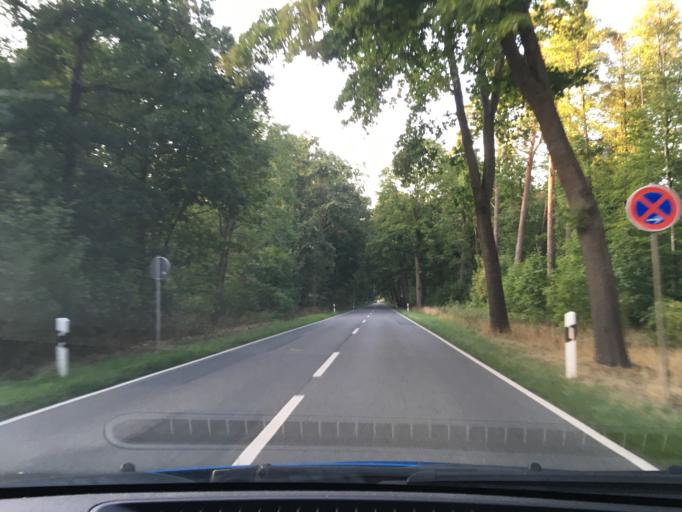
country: DE
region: Lower Saxony
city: Bleckede
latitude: 53.2729
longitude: 10.7434
